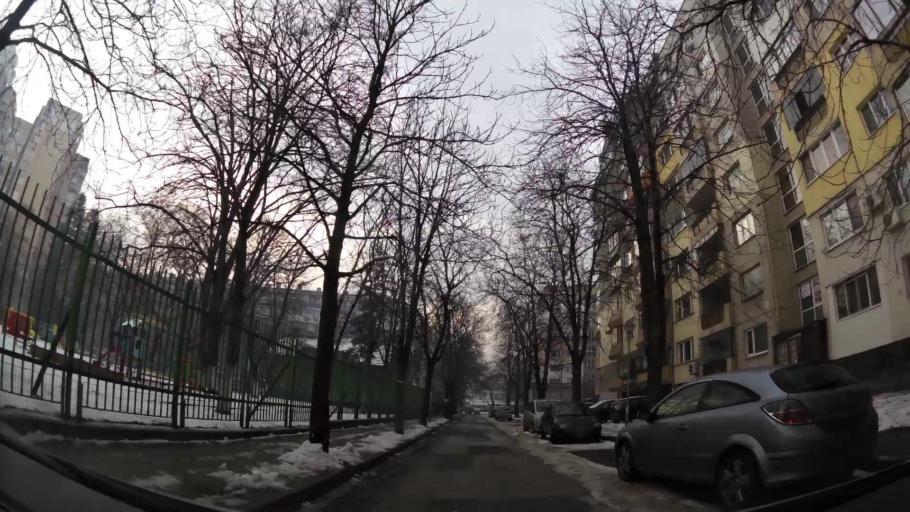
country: BG
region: Sofia-Capital
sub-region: Stolichna Obshtina
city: Sofia
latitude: 42.6948
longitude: 23.2818
